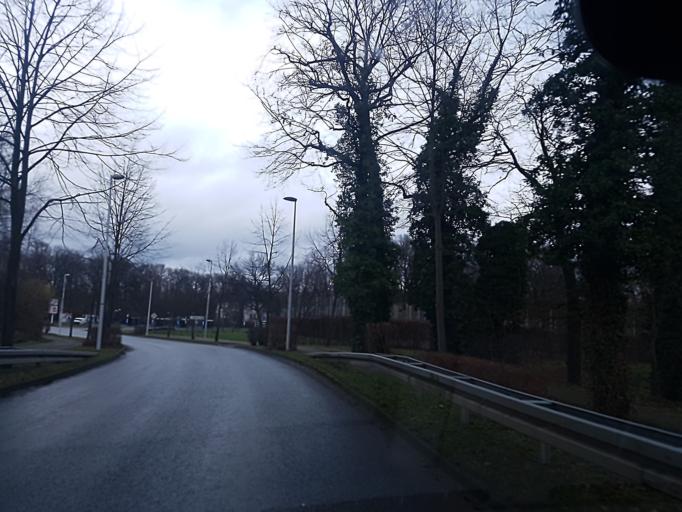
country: DE
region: Brandenburg
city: Bad Liebenwerda
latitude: 51.5133
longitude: 13.4021
